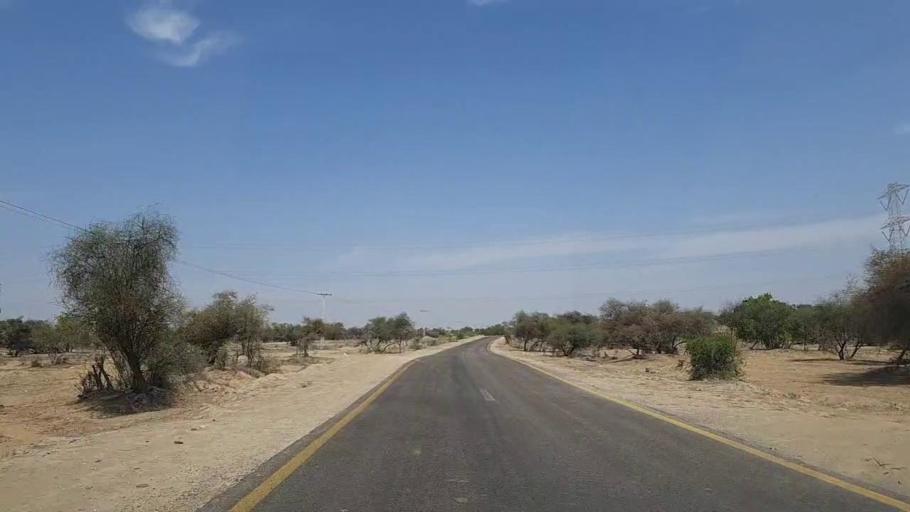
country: PK
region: Sindh
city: Mithi
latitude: 24.8502
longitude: 69.8376
